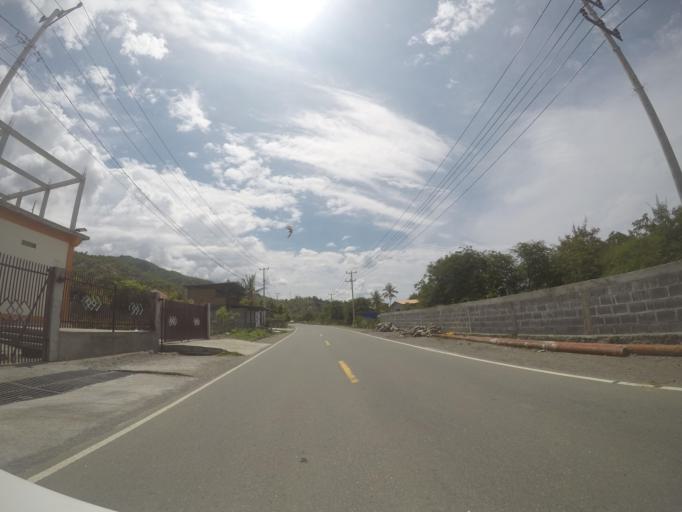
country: TL
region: Liquica
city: Liquica
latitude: -8.5707
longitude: 125.3805
